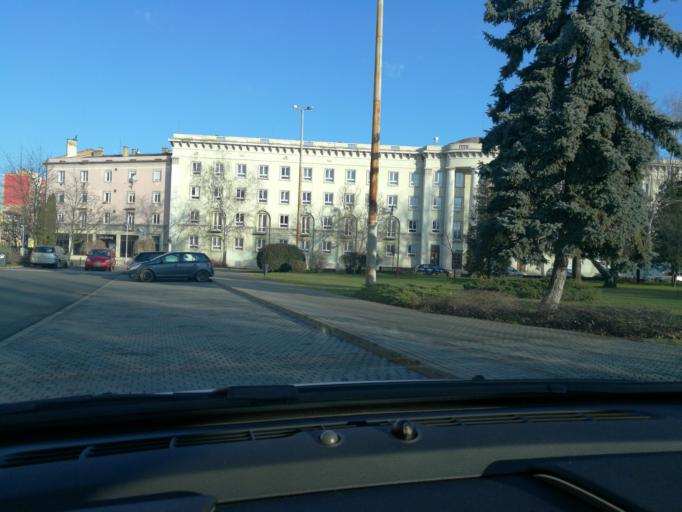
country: HU
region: Szabolcs-Szatmar-Bereg
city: Nyiregyhaza
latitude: 47.9574
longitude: 21.7145
